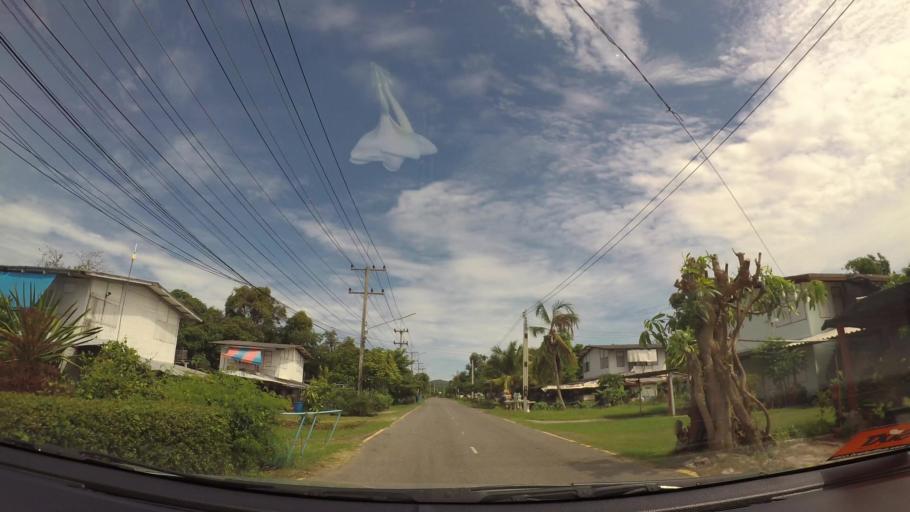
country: TH
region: Chon Buri
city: Sattahip
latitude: 12.6662
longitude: 100.9123
